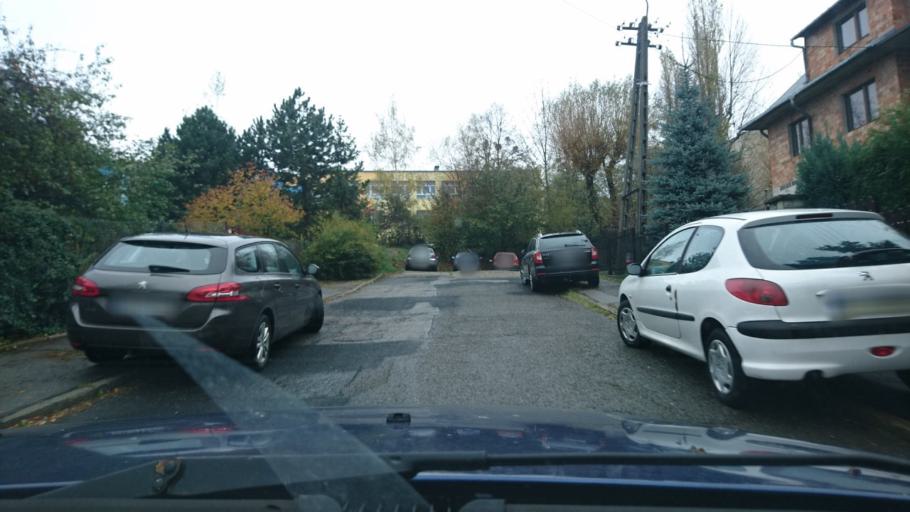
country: PL
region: Silesian Voivodeship
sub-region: Bielsko-Biala
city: Bielsko-Biala
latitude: 49.8037
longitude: 19.0643
